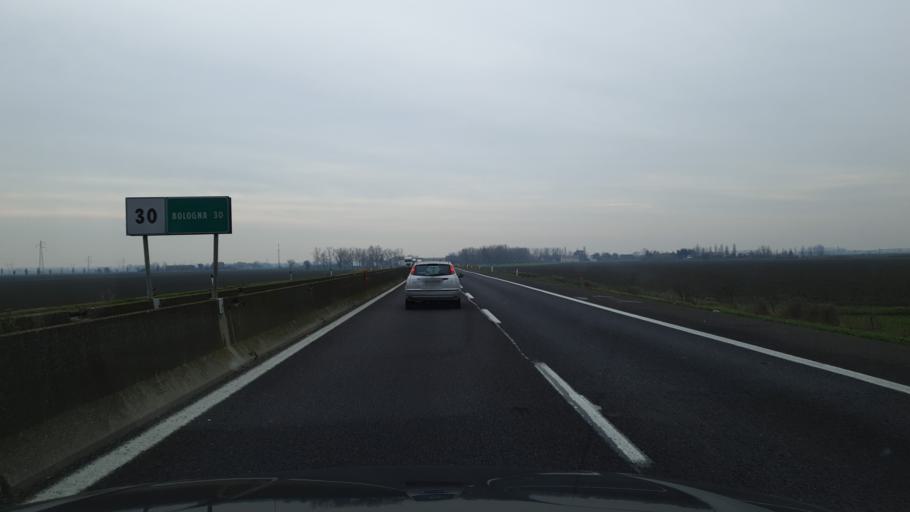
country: IT
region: Emilia-Romagna
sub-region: Provincia di Ferrara
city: Gallo
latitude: 44.7633
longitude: 11.5377
